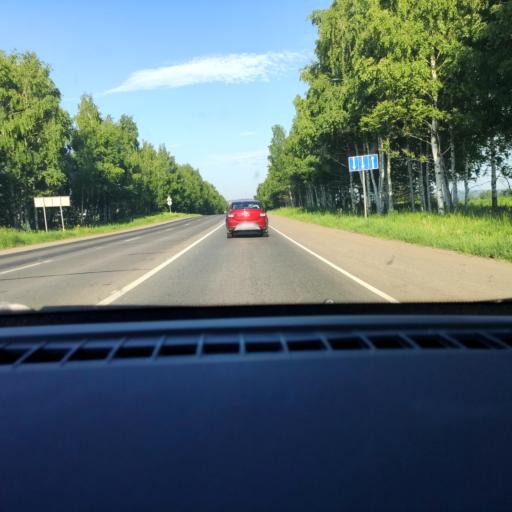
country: RU
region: Udmurtiya
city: Khokhryaki
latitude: 56.9152
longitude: 53.4174
